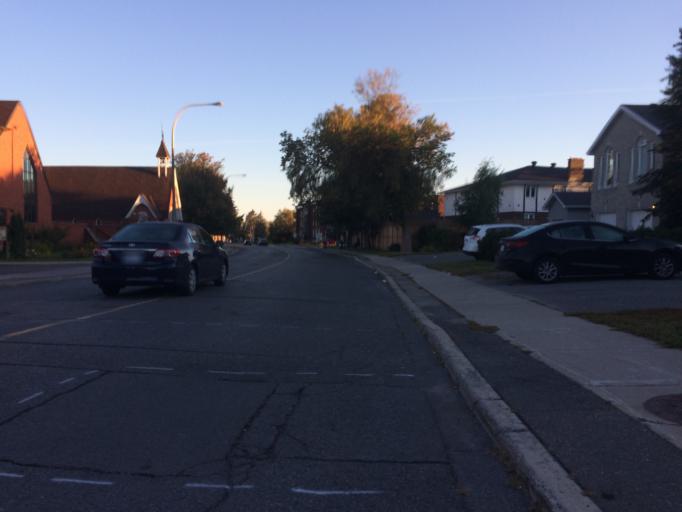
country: CA
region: Ontario
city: Bells Corners
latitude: 45.3216
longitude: -75.8260
